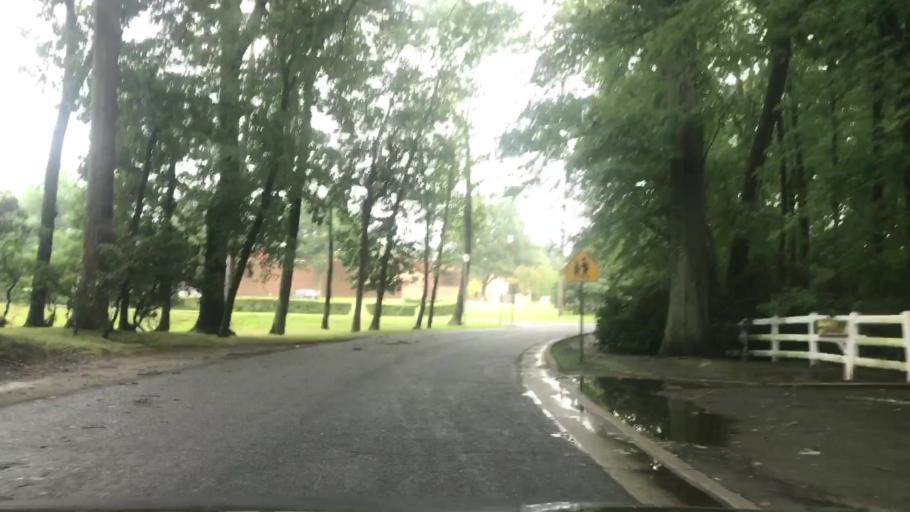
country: US
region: New Jersey
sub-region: Monmouth County
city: Fair Haven
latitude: 40.3502
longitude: -74.0431
